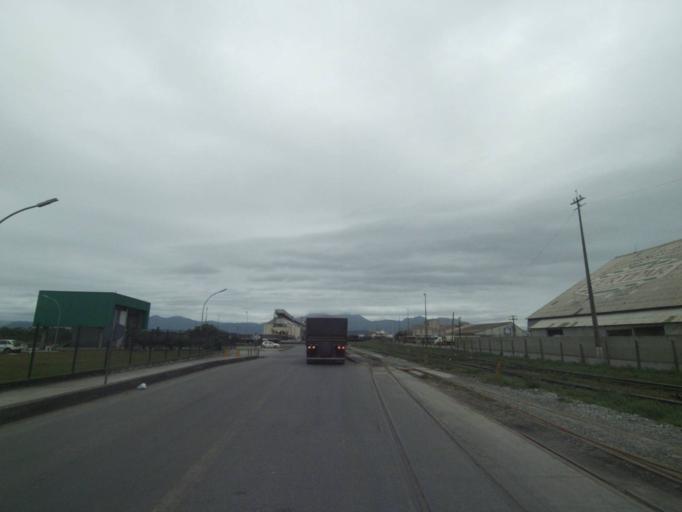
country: BR
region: Parana
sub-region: Paranagua
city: Paranagua
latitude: -25.5380
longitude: -48.5369
